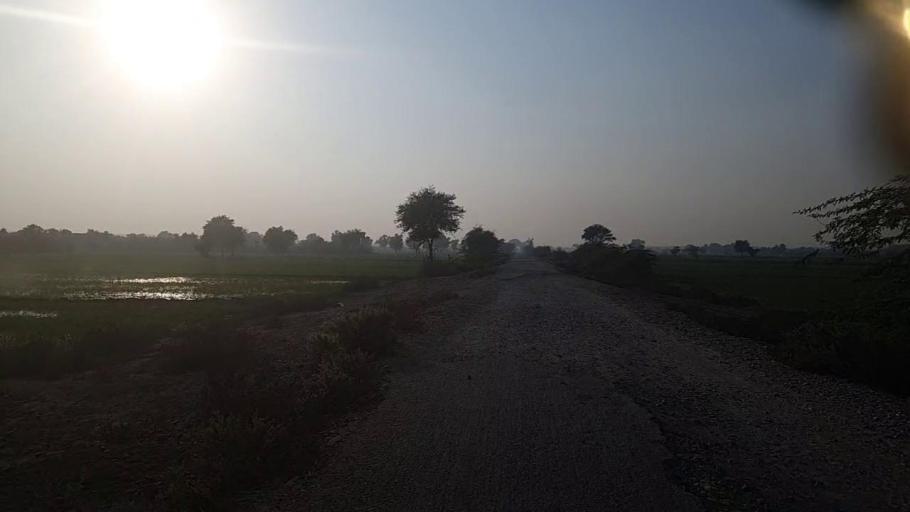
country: PK
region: Sindh
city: Pad Idan
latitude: 26.7201
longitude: 68.4344
